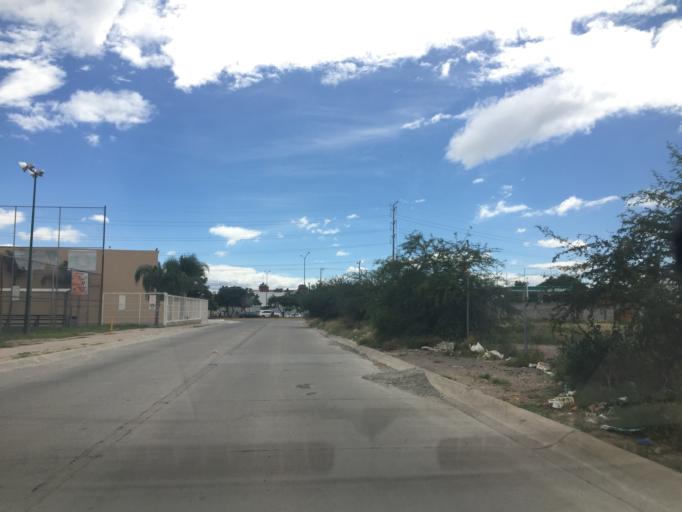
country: MX
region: Guanajuato
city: Leon
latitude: 21.1503
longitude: -101.6620
